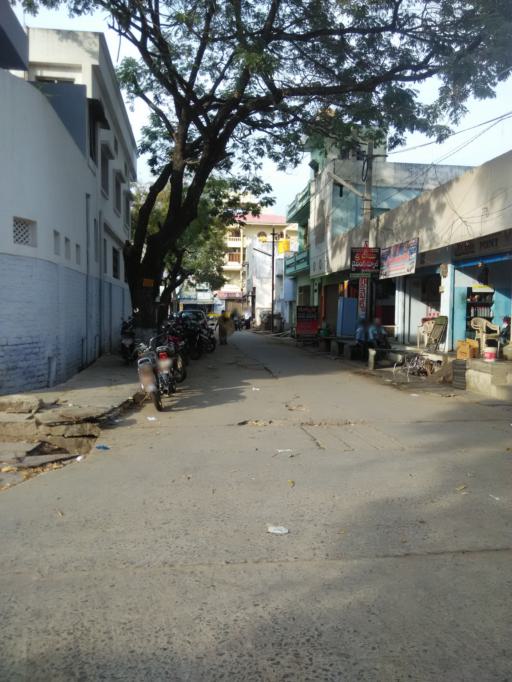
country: IN
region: Andhra Pradesh
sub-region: Kurnool
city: Nandyal
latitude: 15.4863
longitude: 78.4801
